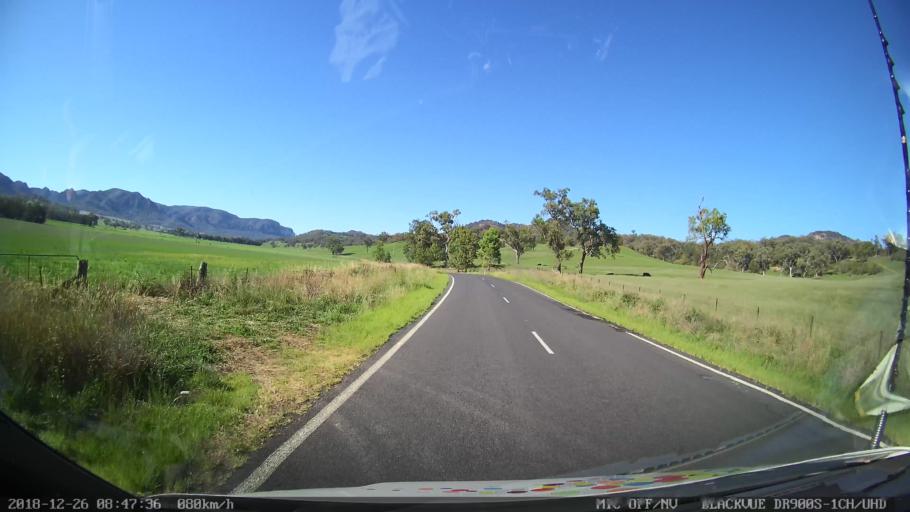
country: AU
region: New South Wales
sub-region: Mid-Western Regional
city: Kandos
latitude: -32.5445
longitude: 150.0903
